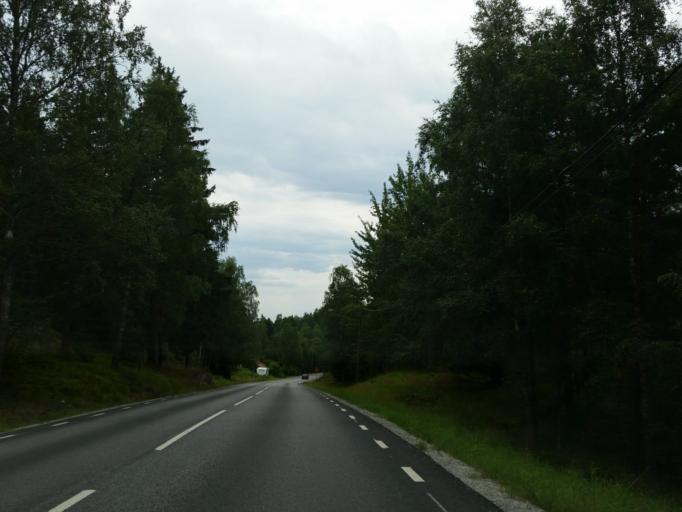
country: SE
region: Stockholm
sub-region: Sodertalje Kommun
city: Soedertaelje
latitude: 59.2189
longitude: 17.6671
